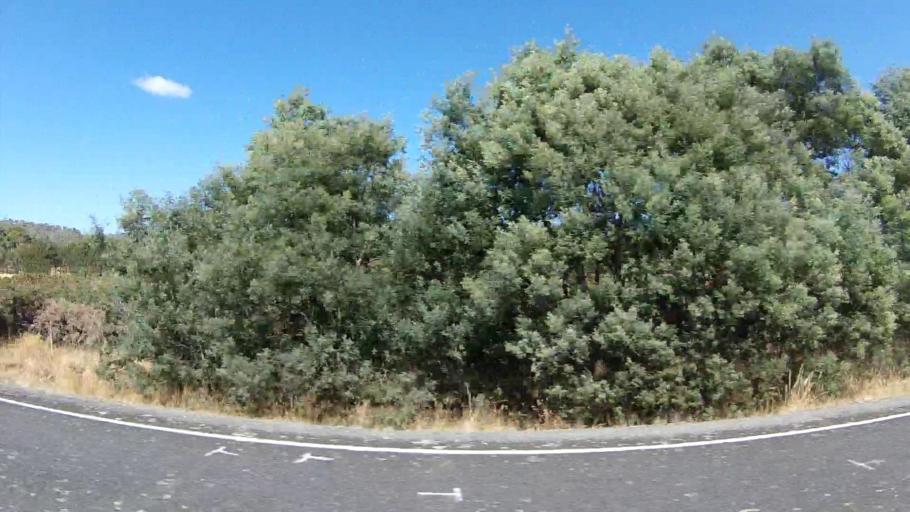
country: AU
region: Tasmania
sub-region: Sorell
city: Sorell
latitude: -42.5943
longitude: 147.7889
